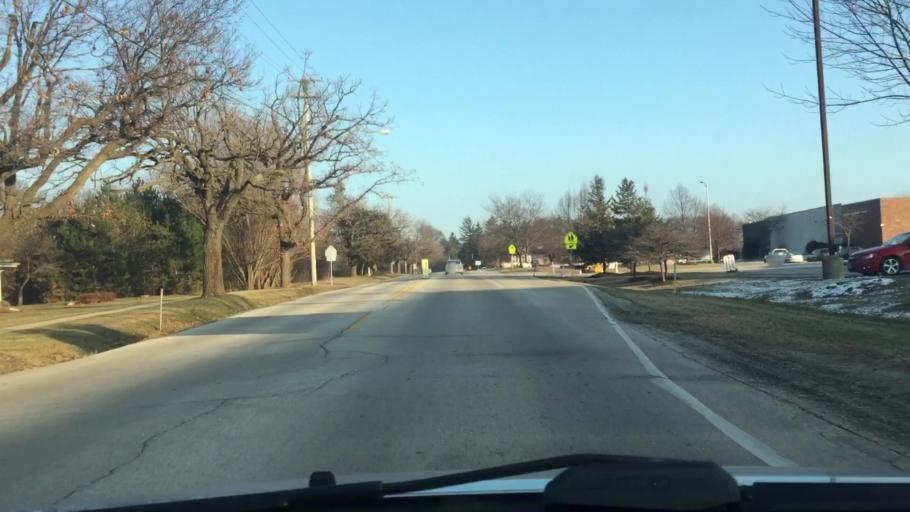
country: US
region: Wisconsin
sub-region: Waukesha County
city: Dousman
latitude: 43.0104
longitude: -88.4666
